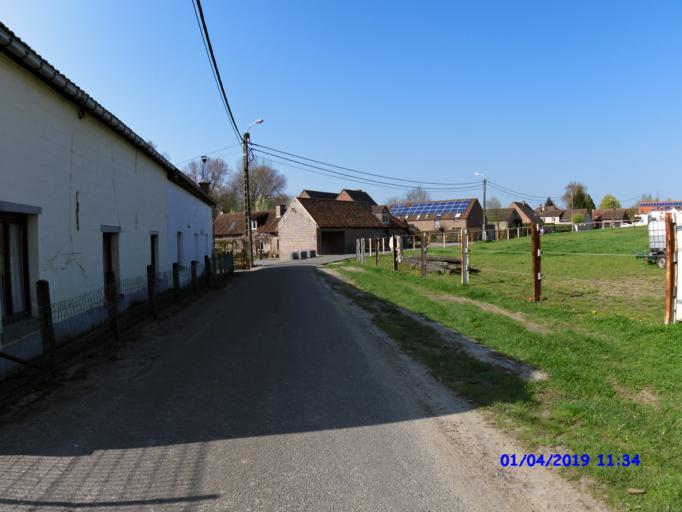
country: BE
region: Flanders
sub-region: Provincie Vlaams-Brabant
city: Ternat
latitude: 50.8735
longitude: 4.1968
